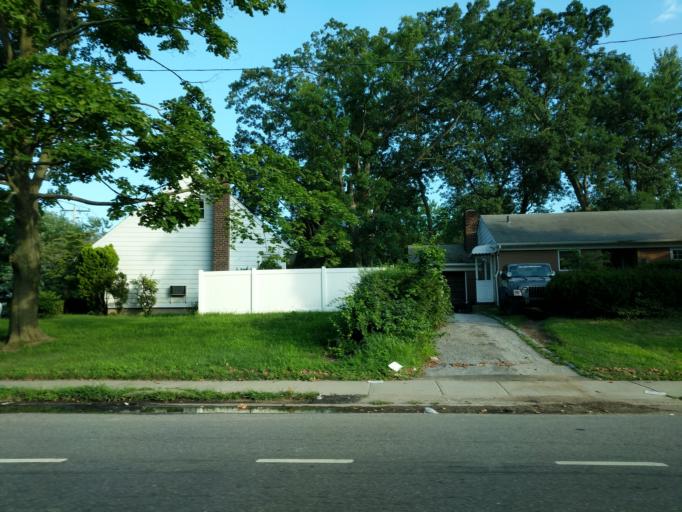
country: US
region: New York
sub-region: Nassau County
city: Hewlett
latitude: 40.6471
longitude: -73.6943
